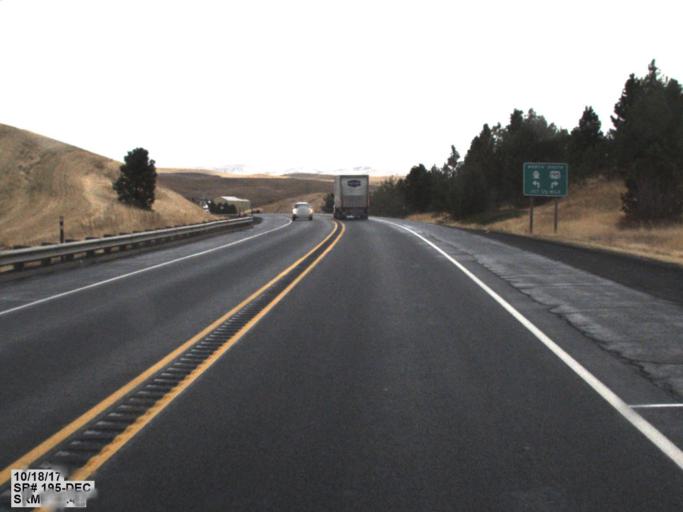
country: US
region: Washington
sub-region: Whitman County
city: Pullman
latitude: 46.7097
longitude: -117.2140
